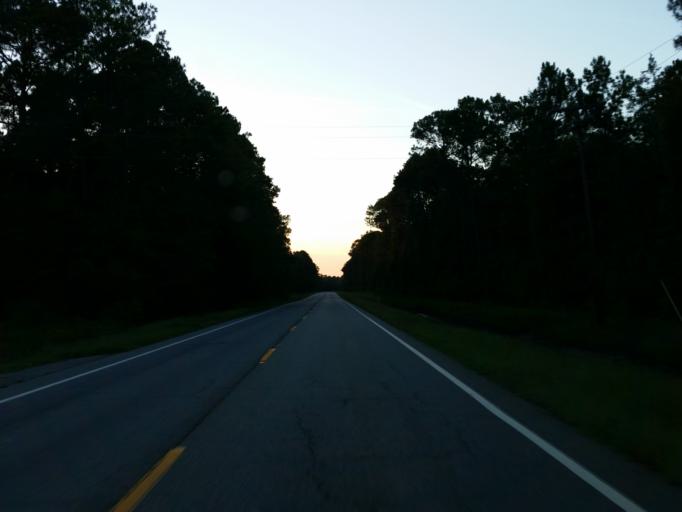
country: US
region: Georgia
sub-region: Berrien County
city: Nashville
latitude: 31.2318
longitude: -83.3054
